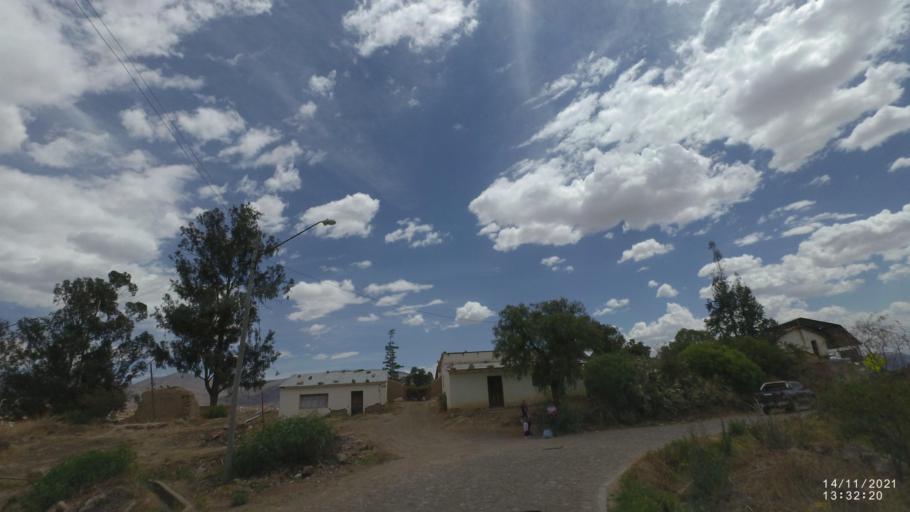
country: BO
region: Cochabamba
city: Colomi
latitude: -17.3966
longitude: -65.9829
